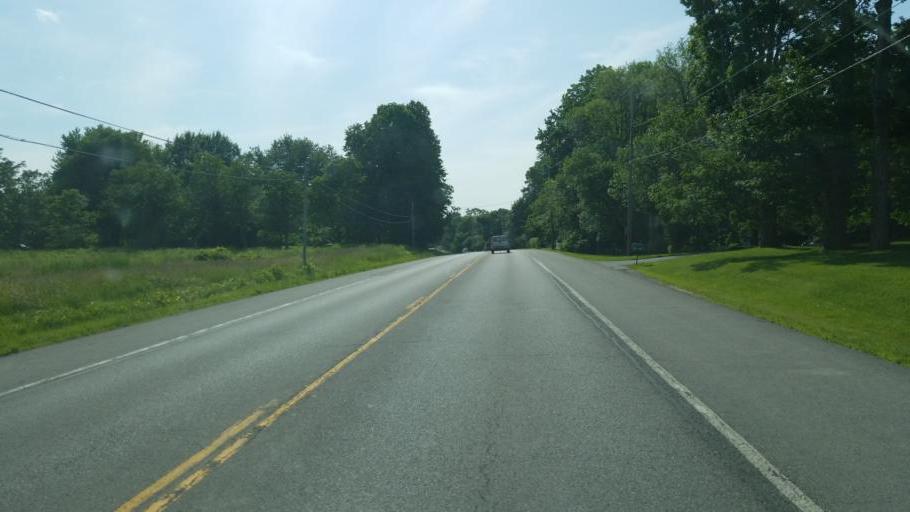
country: US
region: New York
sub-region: Monroe County
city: Honeoye Falls
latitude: 42.9057
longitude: -77.5314
